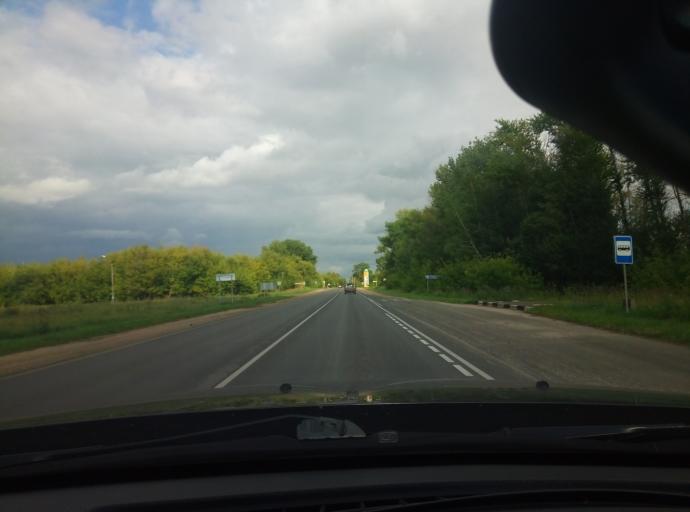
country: RU
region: Tula
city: Kimovsk
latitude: 53.9721
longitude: 38.5005
